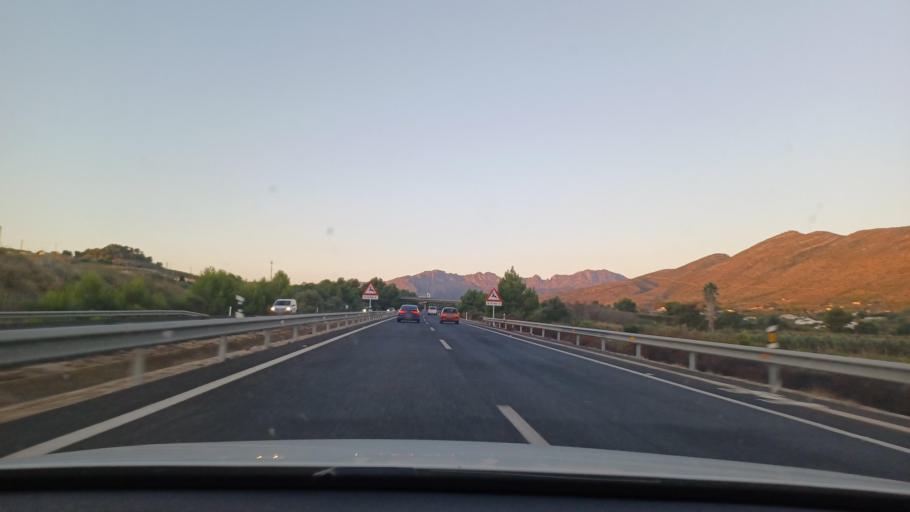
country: ES
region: Valencia
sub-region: Provincia de Alicante
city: Benissa
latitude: 38.7162
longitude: 0.0379
